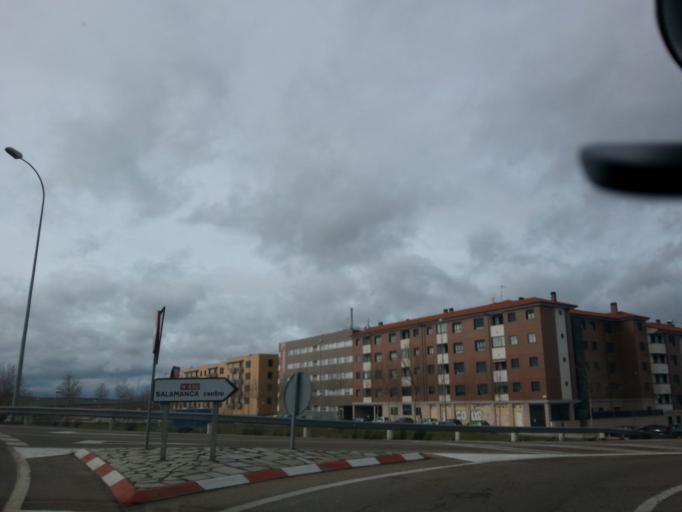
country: ES
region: Castille and Leon
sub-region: Provincia de Salamanca
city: Carbajosa de la Sagrada
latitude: 40.9419
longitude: -5.6686
